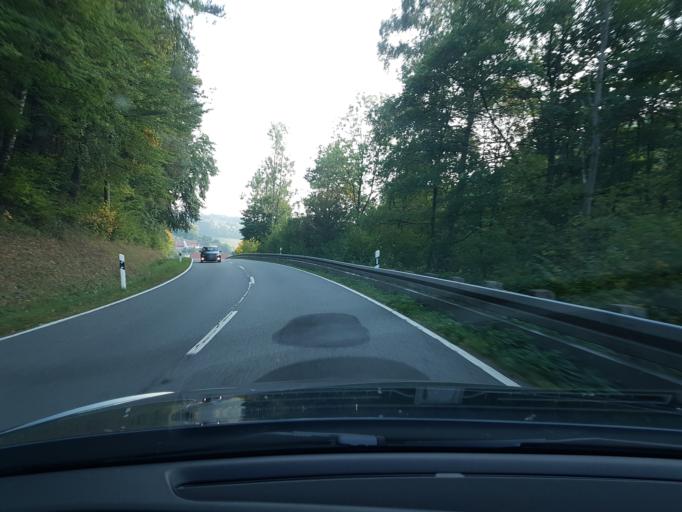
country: DE
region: Hesse
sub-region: Regierungsbezirk Darmstadt
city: Beerfelden
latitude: 49.5444
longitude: 8.9694
